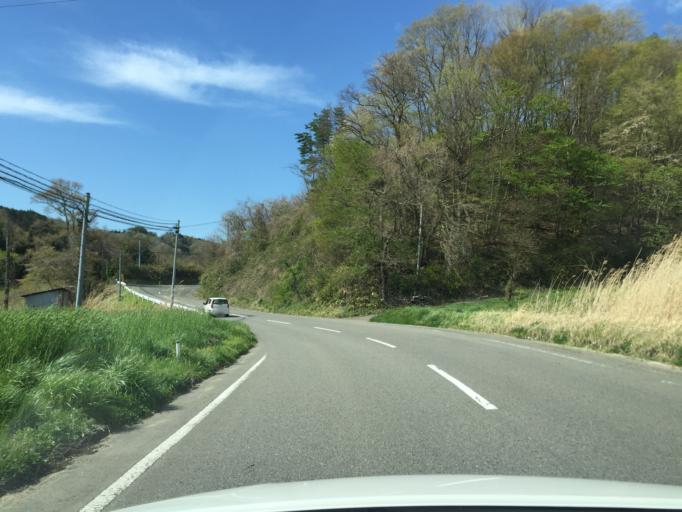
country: JP
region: Fukushima
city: Funehikimachi-funehiki
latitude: 37.5494
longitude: 140.6405
